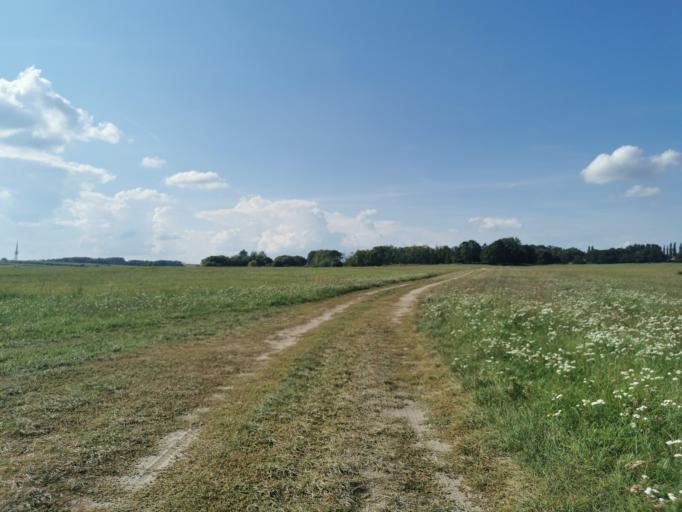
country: SK
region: Trnavsky
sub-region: Okres Senica
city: Senica
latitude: 48.5960
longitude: 17.2523
